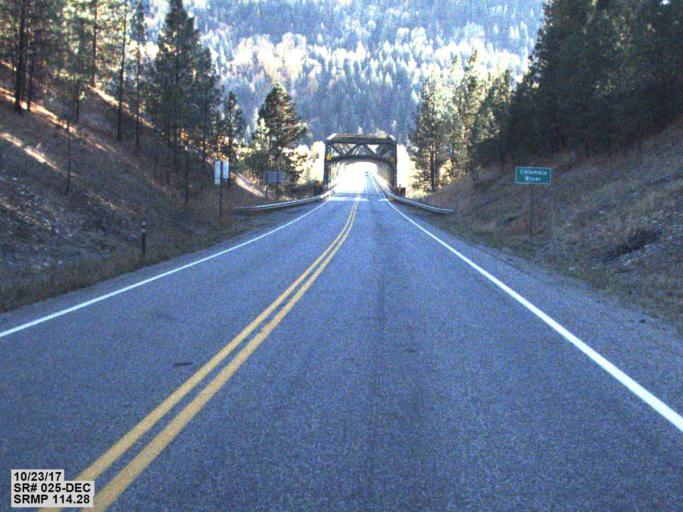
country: CA
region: British Columbia
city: Rossland
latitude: 48.9252
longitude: -117.7774
